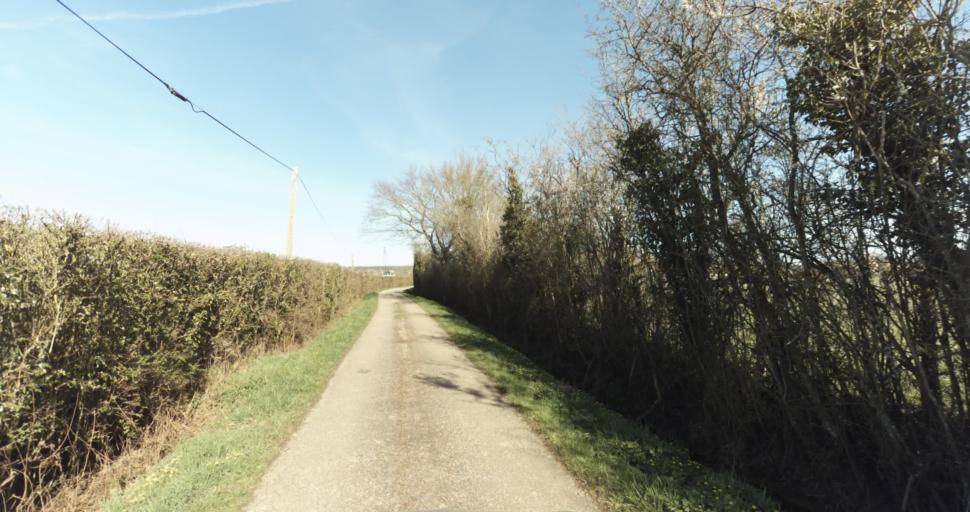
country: FR
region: Lower Normandy
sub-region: Departement du Calvados
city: Saint-Pierre-sur-Dives
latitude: 49.0322
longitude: 0.0125
